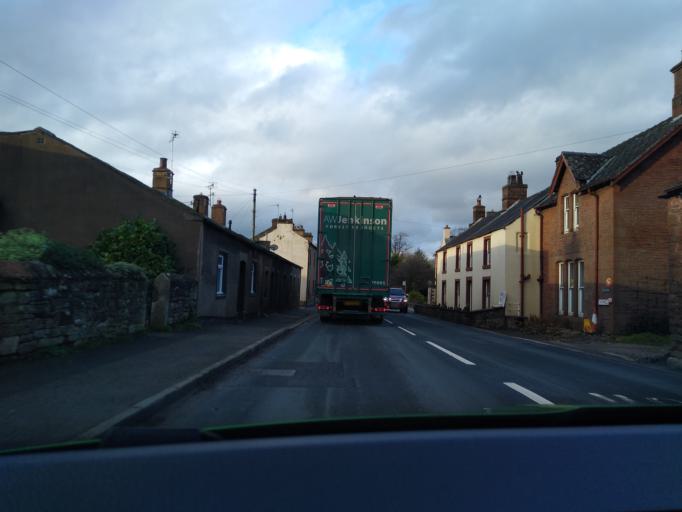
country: GB
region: England
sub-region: Cumbria
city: Penrith
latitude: 54.6495
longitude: -2.7404
